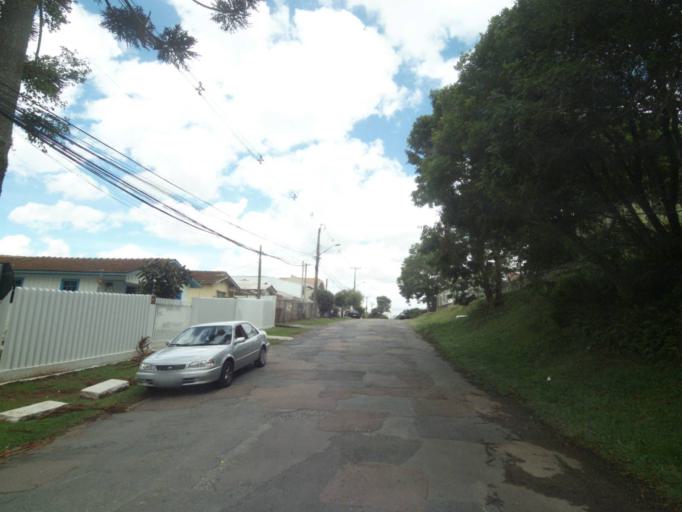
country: BR
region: Parana
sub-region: Curitiba
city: Curitiba
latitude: -25.4326
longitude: -49.3232
